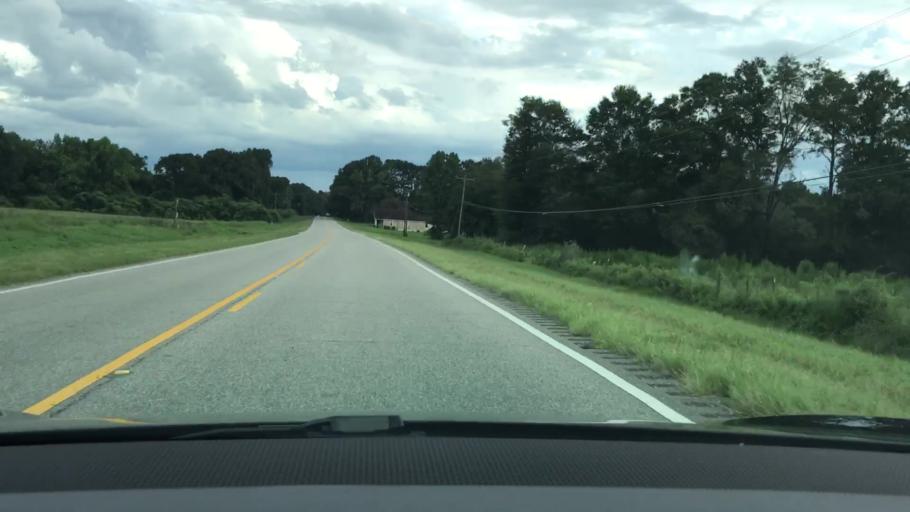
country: US
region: Alabama
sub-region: Coffee County
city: Elba
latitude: 31.5851
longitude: -86.0002
